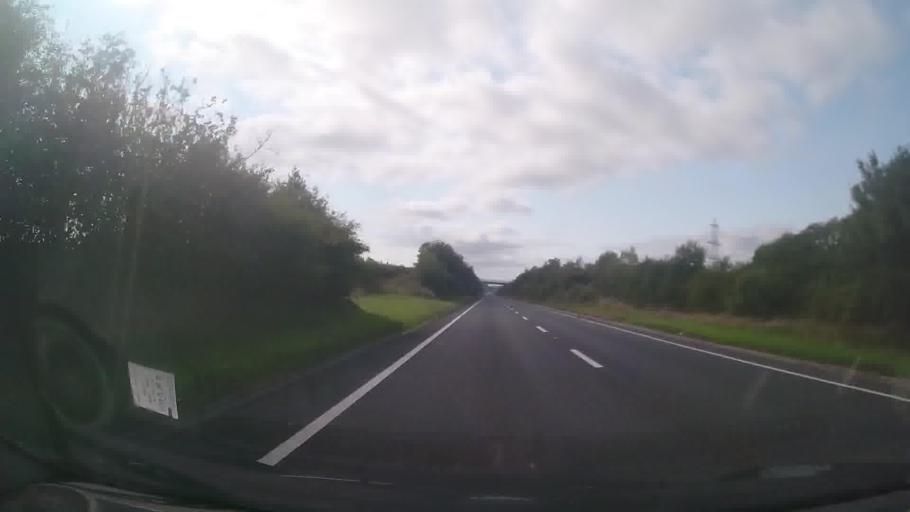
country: GB
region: Wales
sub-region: Pembrokeshire
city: Jeffreyston
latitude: 51.6964
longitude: -4.7907
